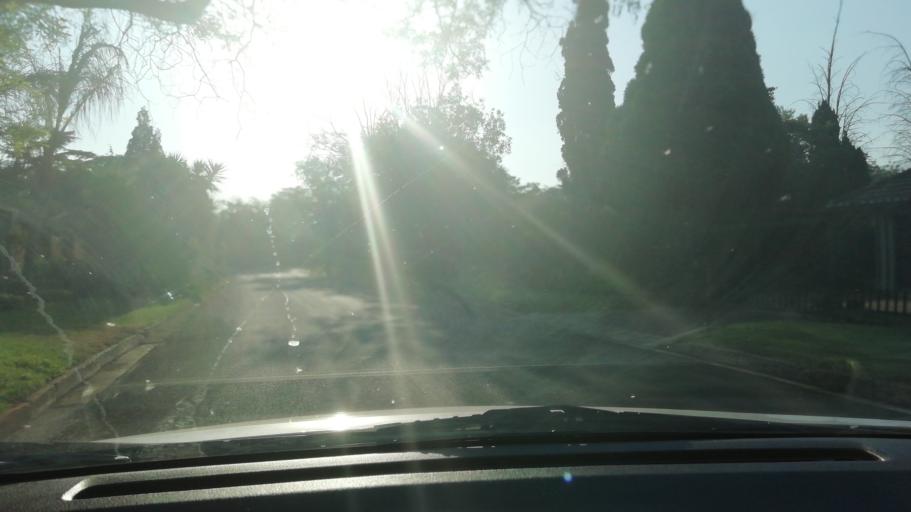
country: ZA
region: Gauteng
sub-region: Ekurhuleni Metropolitan Municipality
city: Benoni
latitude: -26.1808
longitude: 28.2880
